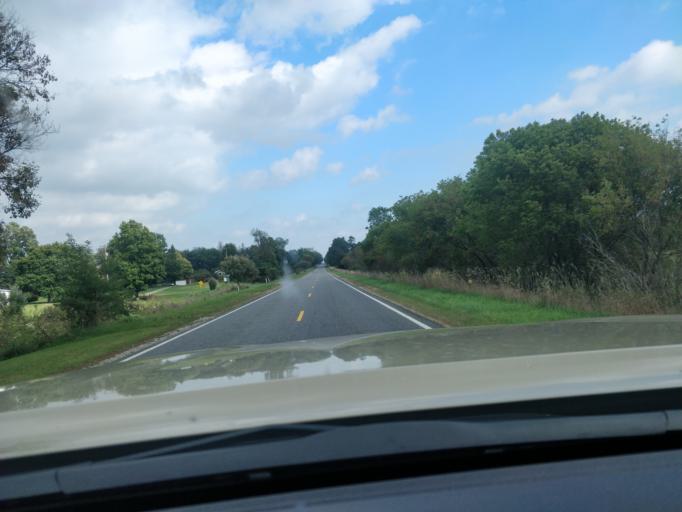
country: US
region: Michigan
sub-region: Ionia County
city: Saranac
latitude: 42.8861
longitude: -85.2619
